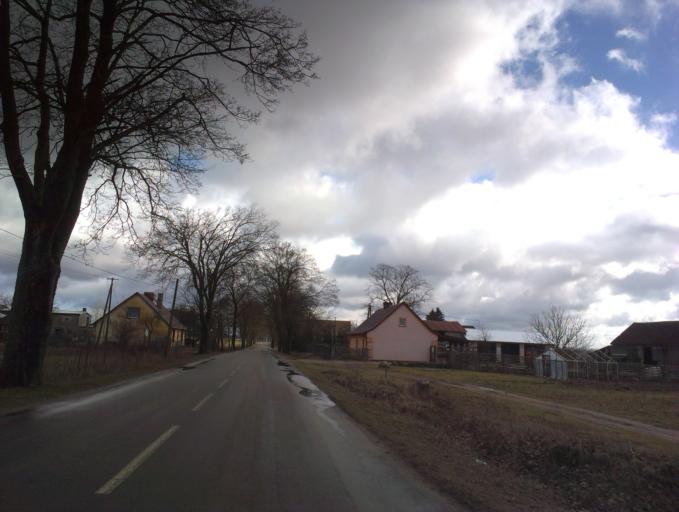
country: PL
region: Pomeranian Voivodeship
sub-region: Powiat czluchowski
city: Czarne
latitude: 53.6872
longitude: 16.9720
